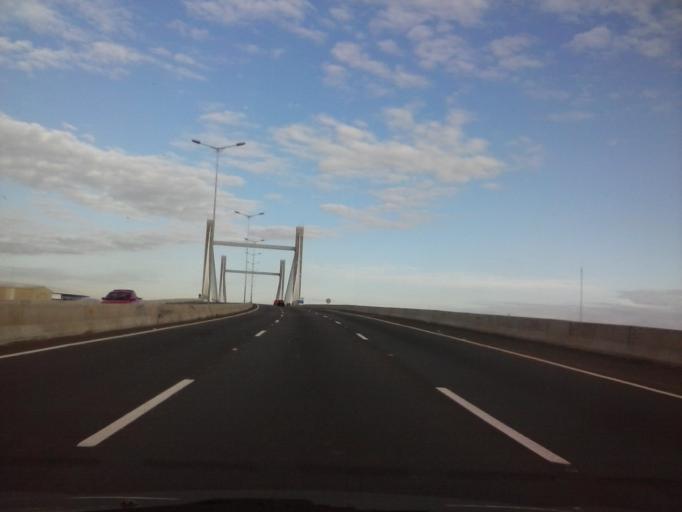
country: BR
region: Rio Grande do Sul
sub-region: Canoas
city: Canoas
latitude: -29.9683
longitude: -51.2013
